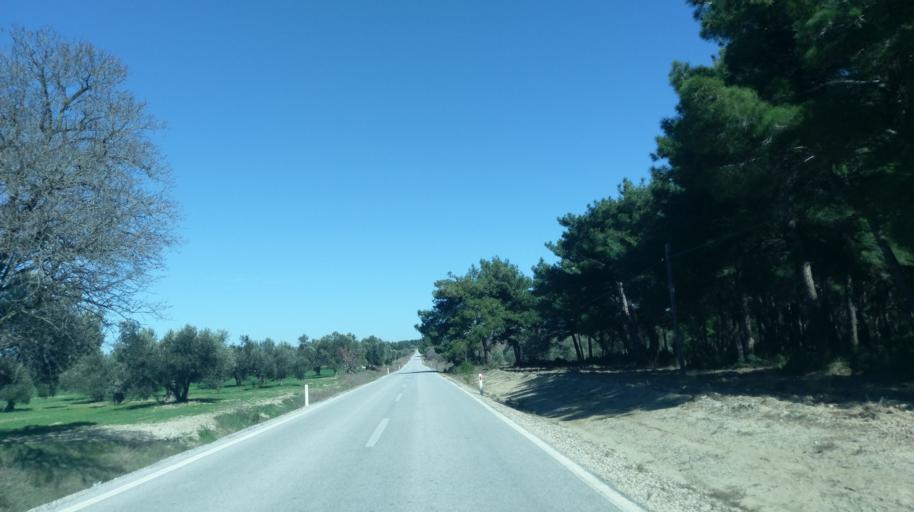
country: TR
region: Canakkale
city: Intepe
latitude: 40.0678
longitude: 26.2063
